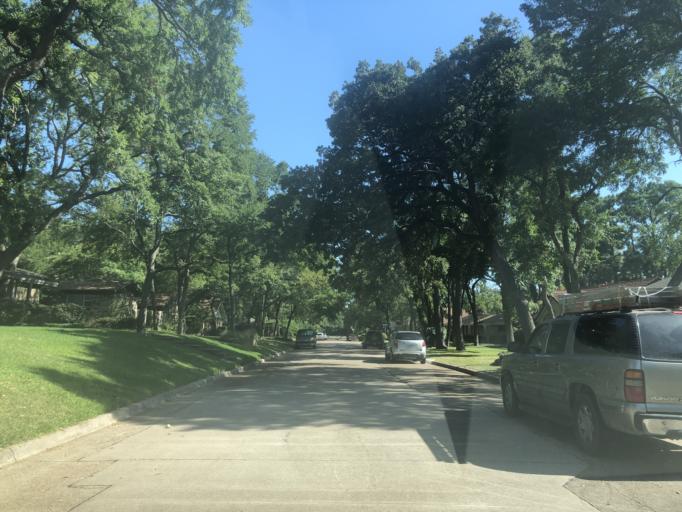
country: US
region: Texas
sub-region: Dallas County
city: Grand Prairie
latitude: 32.7670
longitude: -97.0155
